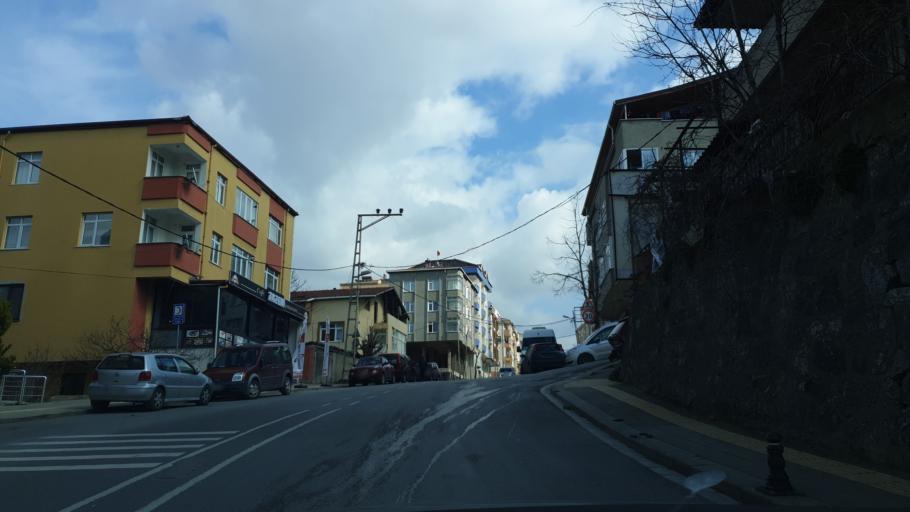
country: TR
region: Istanbul
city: Pendik
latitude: 40.8693
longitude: 29.2861
